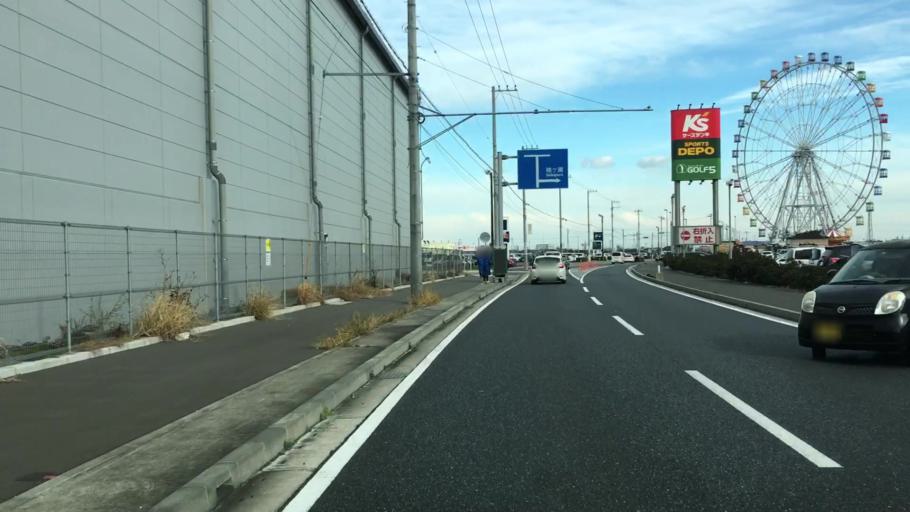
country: JP
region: Chiba
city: Kisarazu
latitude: 35.4390
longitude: 139.9298
